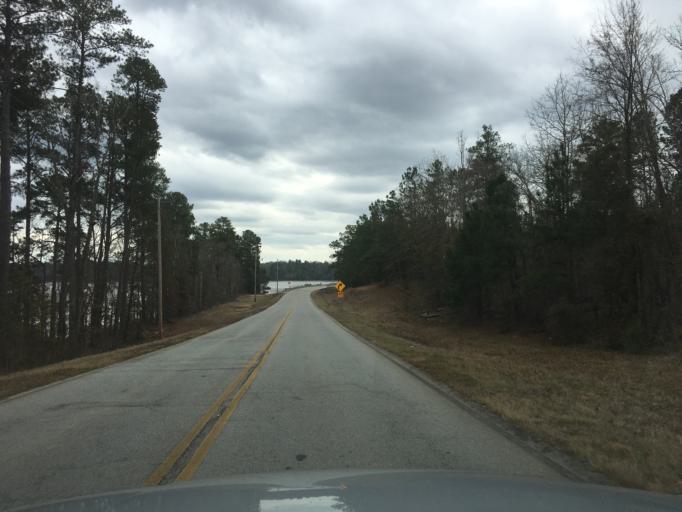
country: US
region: Georgia
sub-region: Lincoln County
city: Lincolnton
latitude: 33.8312
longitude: -82.4066
